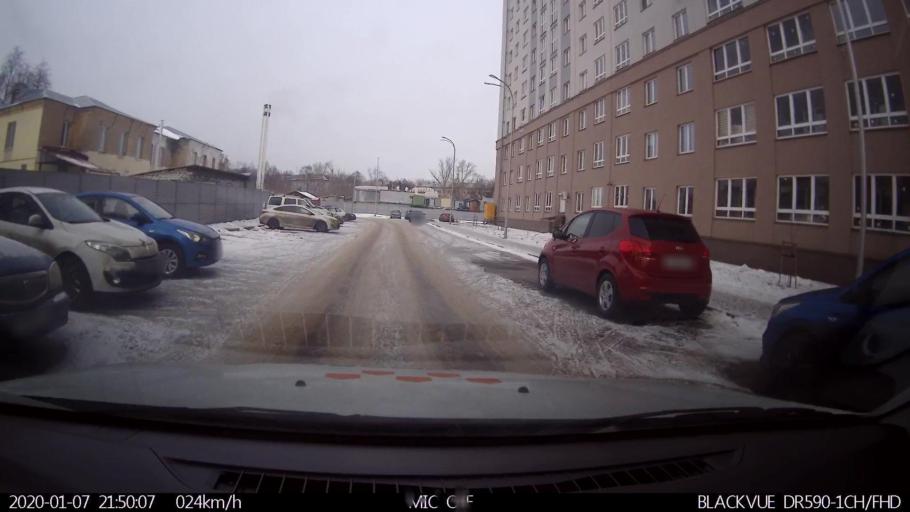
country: RU
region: Nizjnij Novgorod
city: Nizhniy Novgorod
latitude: 56.3158
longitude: 43.8905
